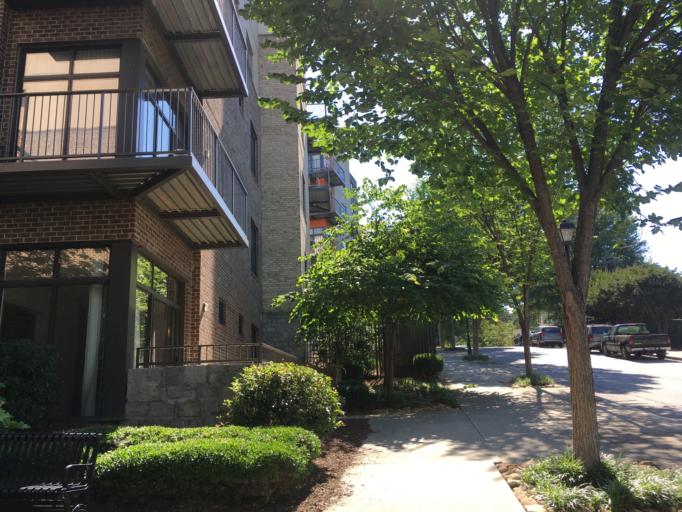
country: US
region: Georgia
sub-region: Fulton County
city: Atlanta
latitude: 33.7695
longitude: -84.3669
